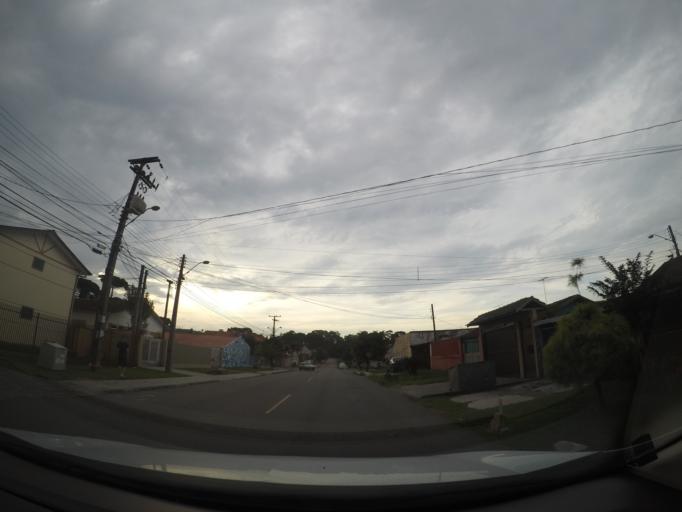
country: BR
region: Parana
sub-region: Sao Jose Dos Pinhais
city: Sao Jose dos Pinhais
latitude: -25.5118
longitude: -49.2407
